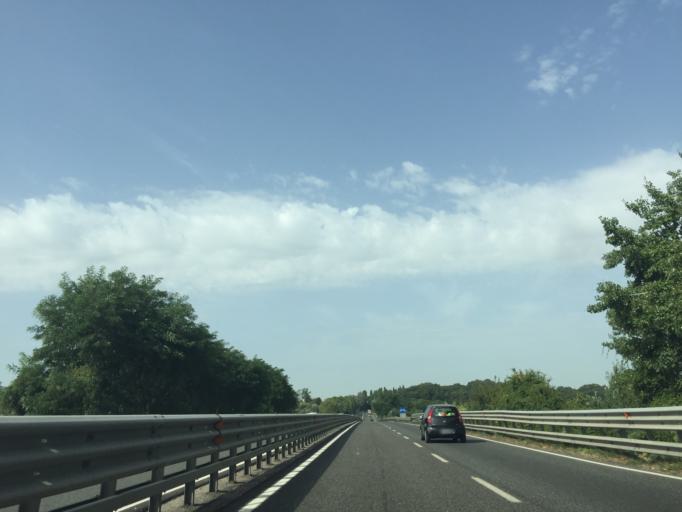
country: IT
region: Tuscany
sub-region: Province of Pisa
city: San Miniato
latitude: 43.6916
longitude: 10.7847
